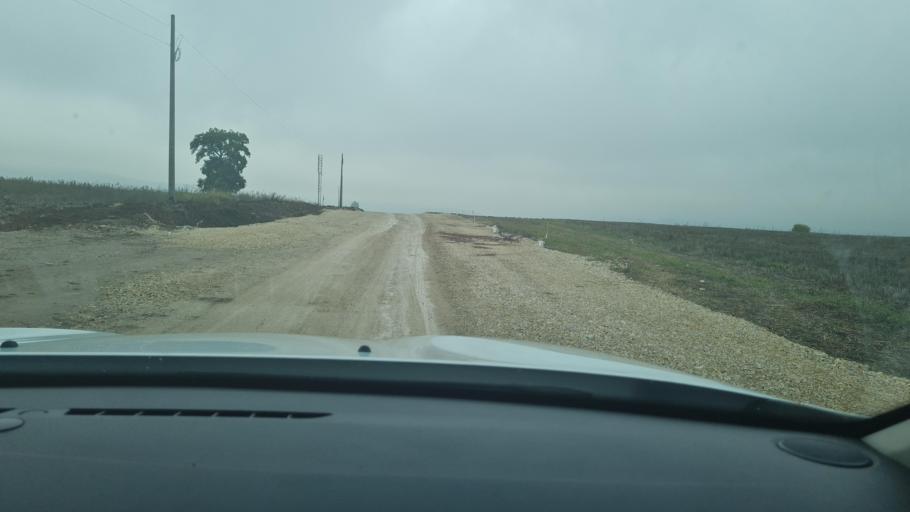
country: MK
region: Opstina Lipkovo
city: Matejche
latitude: 42.1139
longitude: 21.6105
